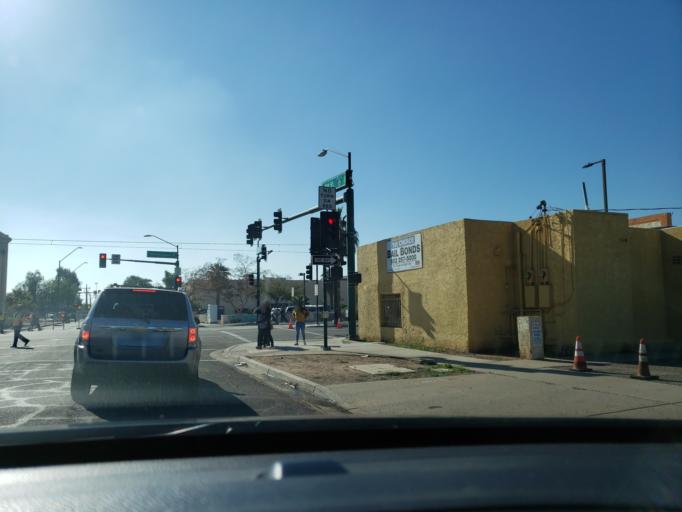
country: US
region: Arizona
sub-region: Maricopa County
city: Phoenix
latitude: 33.4486
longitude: -112.0621
